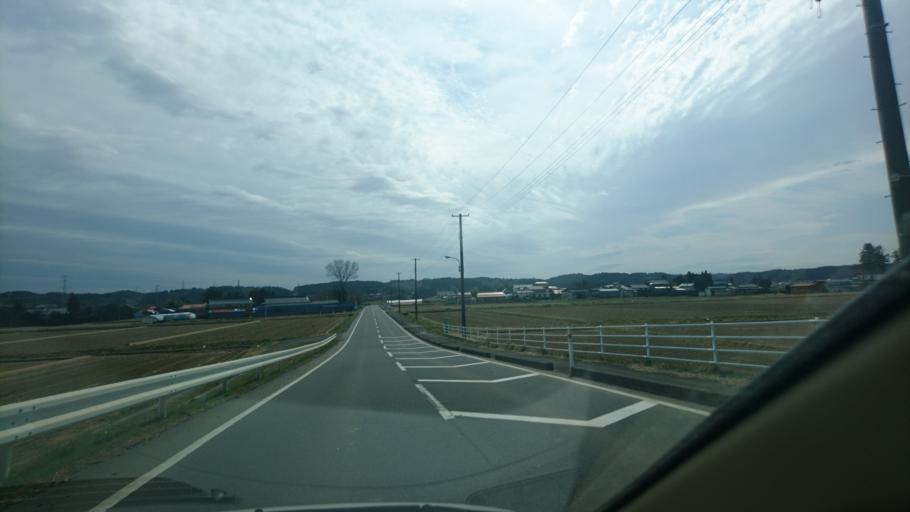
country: JP
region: Miyagi
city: Furukawa
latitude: 38.7431
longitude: 140.9724
